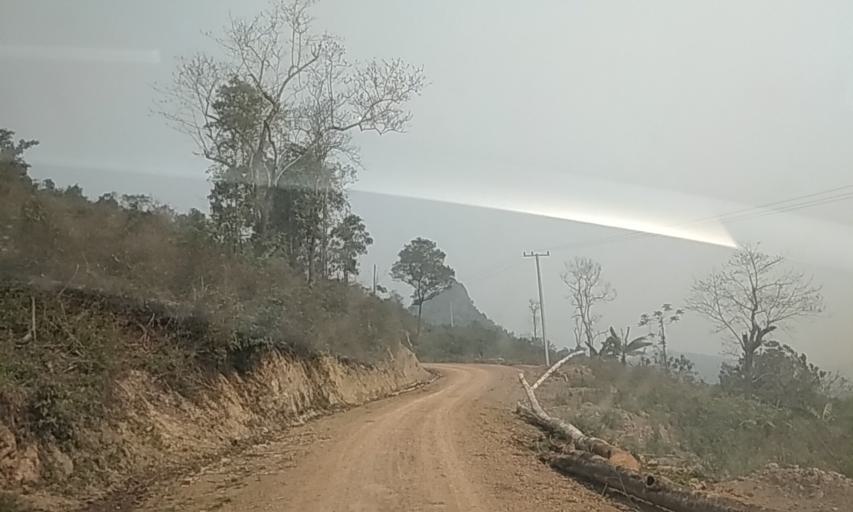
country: VN
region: Huyen Dien Bien
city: Dien Bien Phu
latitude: 21.4457
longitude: 102.7662
